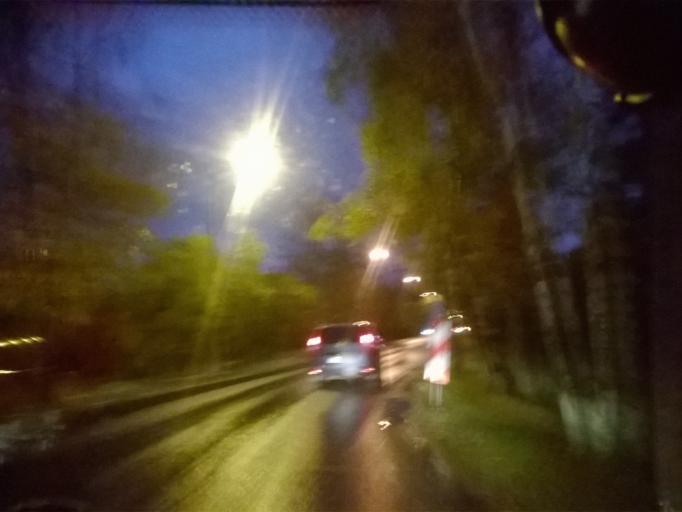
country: EE
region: Harju
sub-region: Viimsi vald
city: Viimsi
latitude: 59.4927
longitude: 24.8788
